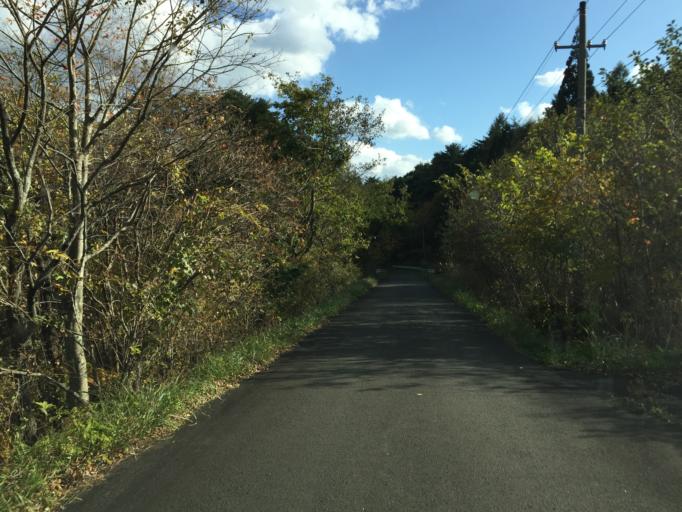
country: JP
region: Fukushima
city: Fukushima-shi
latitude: 37.7150
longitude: 140.3151
